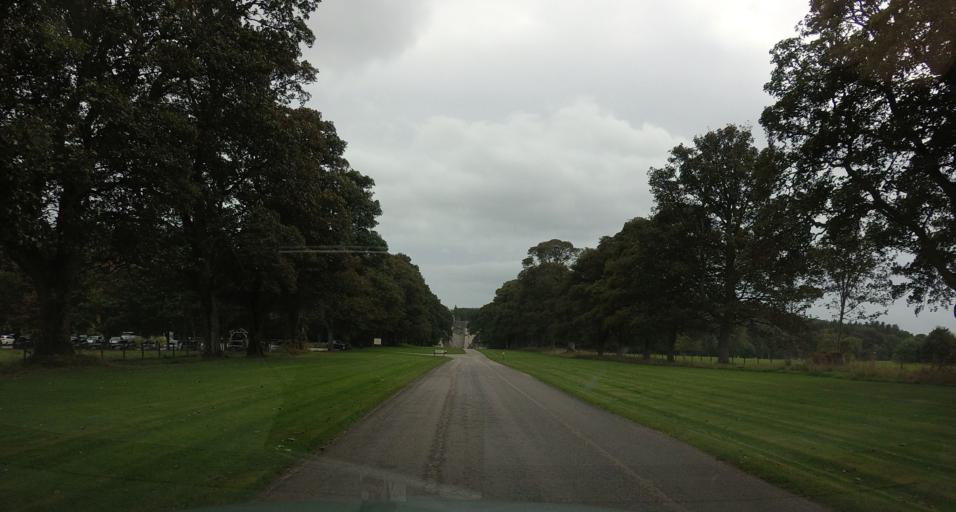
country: GB
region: Scotland
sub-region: Aberdeenshire
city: Kemnay
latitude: 57.2060
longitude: -2.4614
